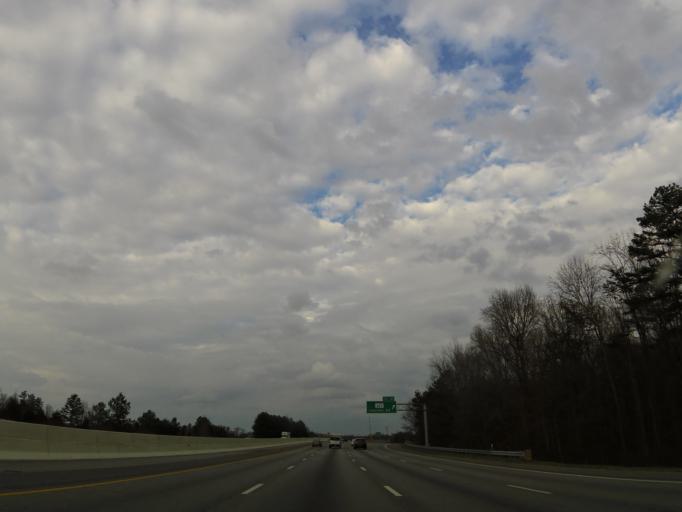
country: US
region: South Carolina
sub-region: Greenville County
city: Mauldin
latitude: 34.7615
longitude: -82.2818
